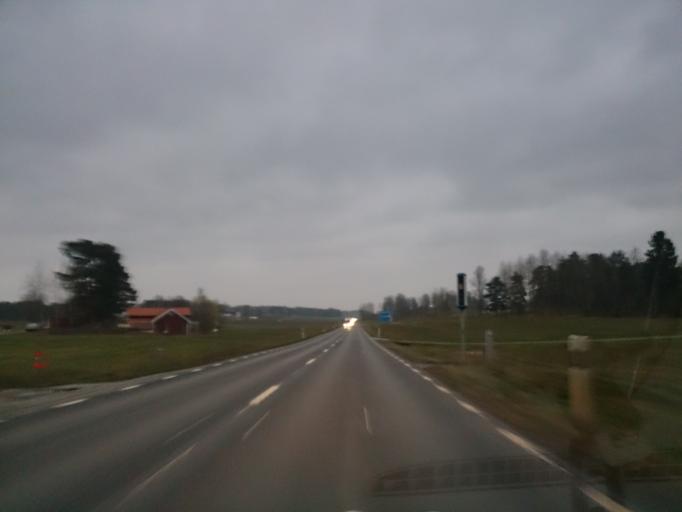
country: SE
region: OEstergoetland
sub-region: Linkopings Kommun
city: Linghem
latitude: 58.3530
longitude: 15.8346
